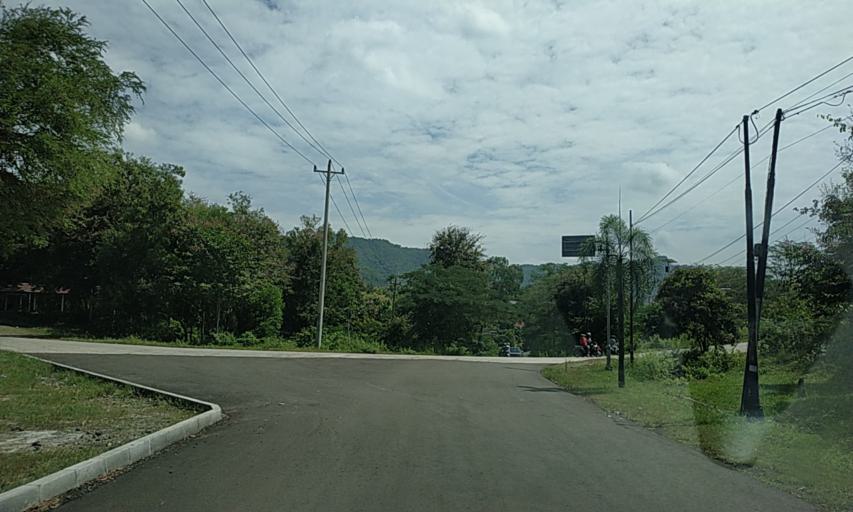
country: ID
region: Central Java
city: Selogiri
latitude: -7.8355
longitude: 110.9228
